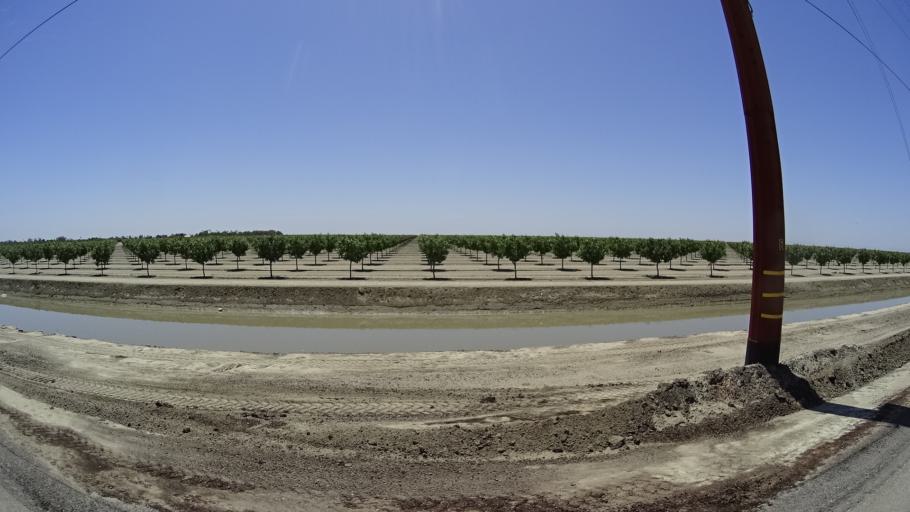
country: US
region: California
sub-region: Kings County
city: Corcoran
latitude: 36.1090
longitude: -119.6021
